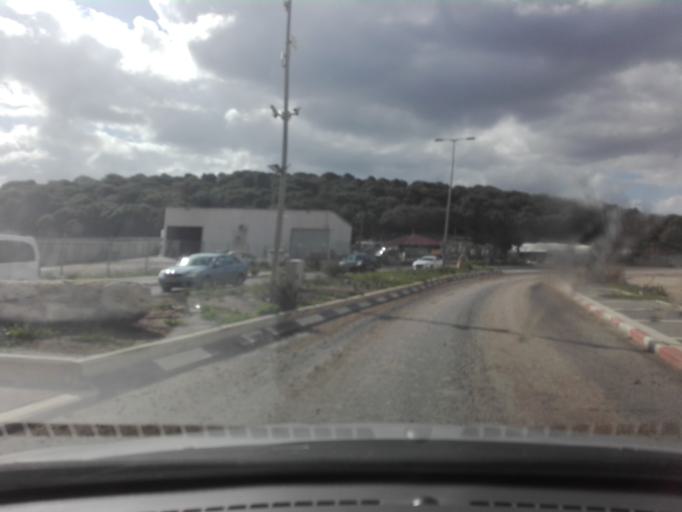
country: IL
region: Haifa
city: Daliyat el Karmil
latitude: 32.6809
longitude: 35.0657
